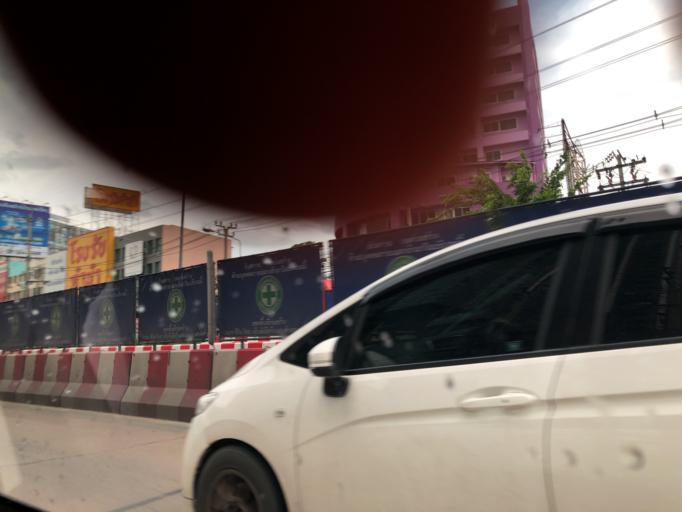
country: TH
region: Nonthaburi
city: Pak Kret
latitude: 13.9040
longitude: 100.5301
